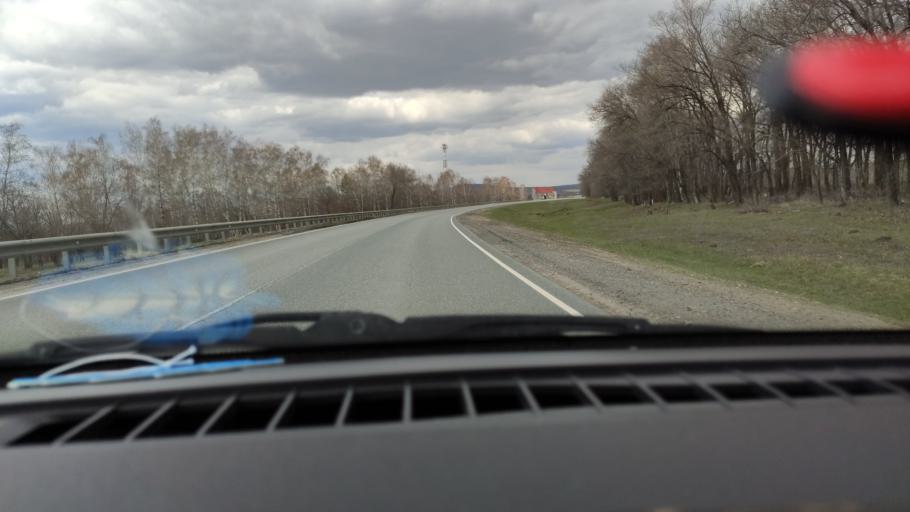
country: RU
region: Saratov
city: Tersa
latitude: 52.0836
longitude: 47.5553
